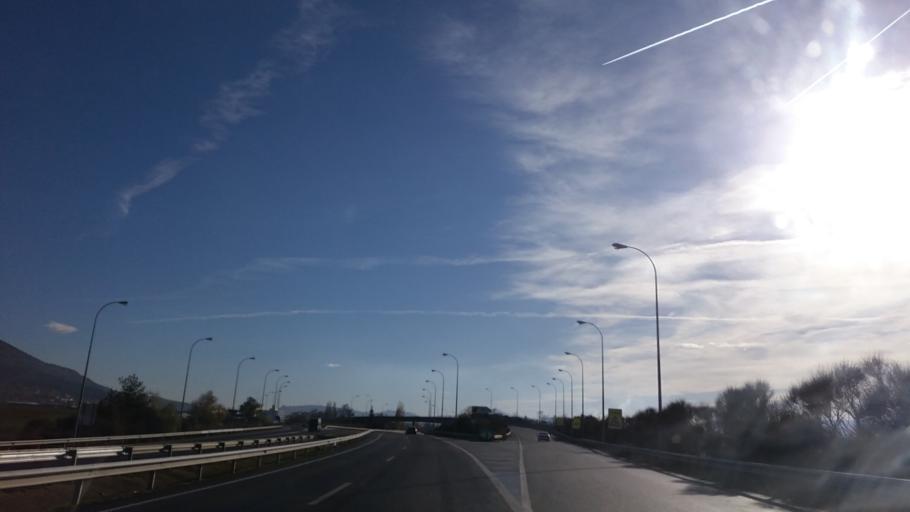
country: ES
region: Navarre
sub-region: Provincia de Navarra
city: Berriobeiti
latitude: 42.8455
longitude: -1.6962
